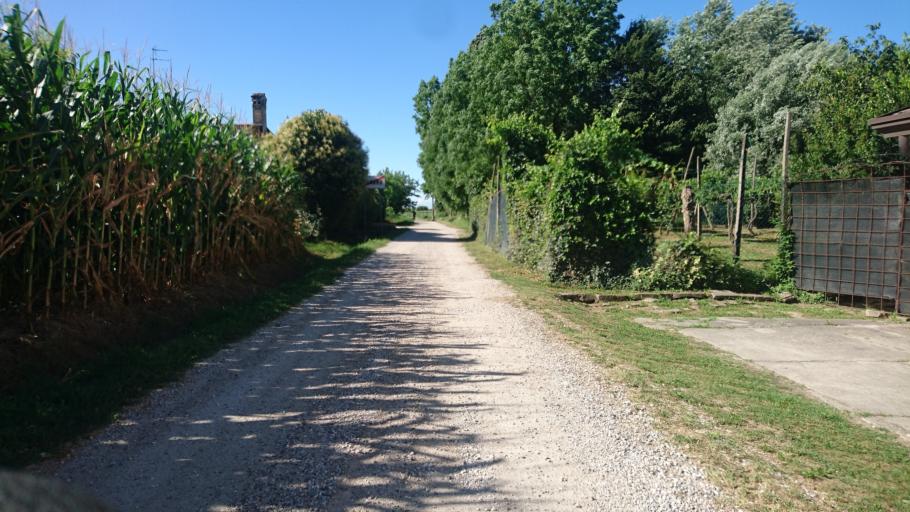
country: IT
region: Veneto
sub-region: Provincia di Padova
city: Legnaro
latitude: 45.3366
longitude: 11.9661
